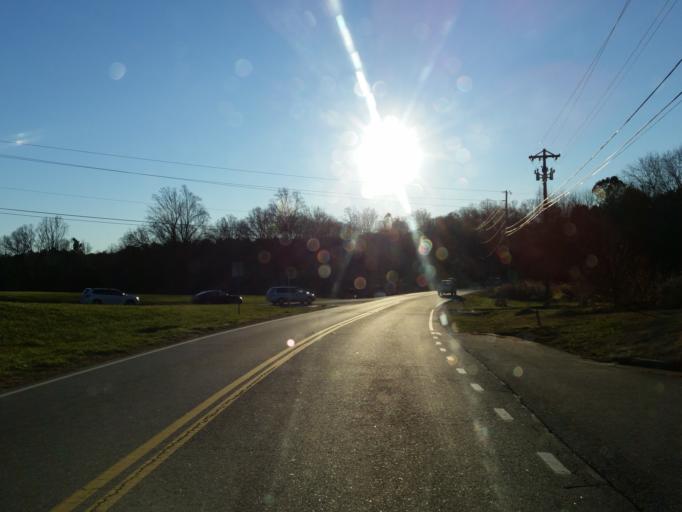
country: US
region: Georgia
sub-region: Cherokee County
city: Holly Springs
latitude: 34.1406
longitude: -84.4557
